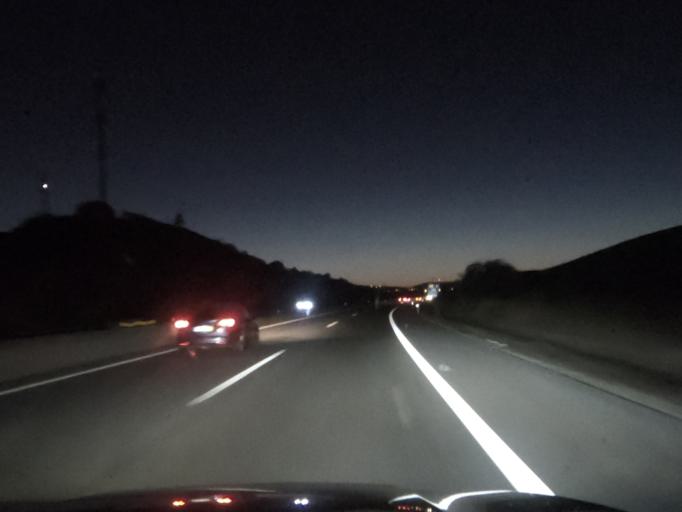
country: PT
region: Faro
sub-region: Loule
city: Vilamoura
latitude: 37.1313
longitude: -8.1030
